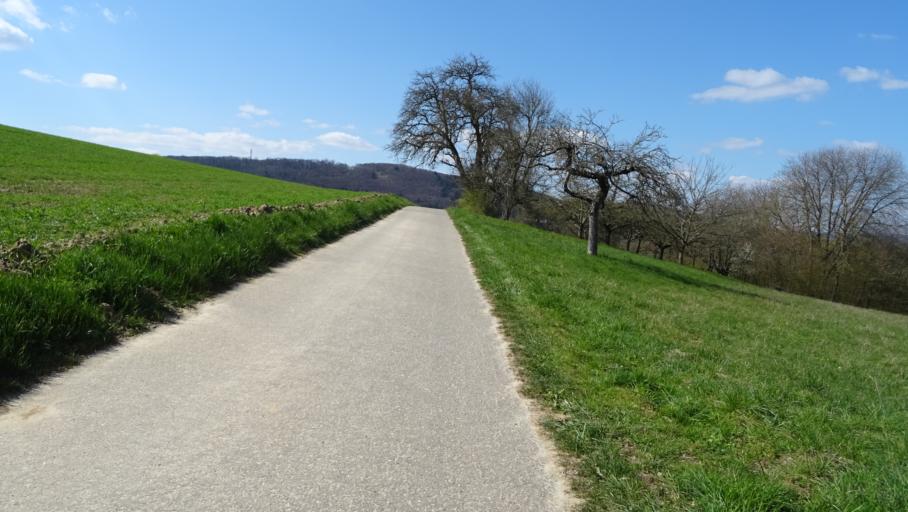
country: DE
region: Baden-Wuerttemberg
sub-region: Karlsruhe Region
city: Neckarzimmern
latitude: 49.3314
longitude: 9.1167
